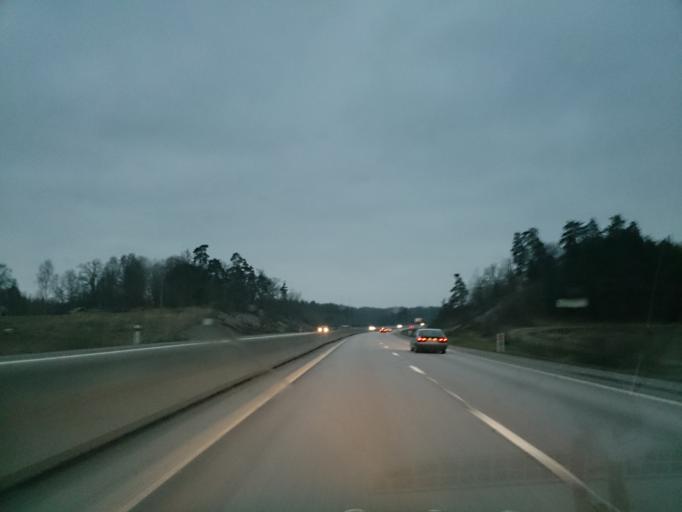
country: SE
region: OEstergoetland
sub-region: Norrkopings Kommun
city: Kimstad
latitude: 58.5577
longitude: 16.0595
